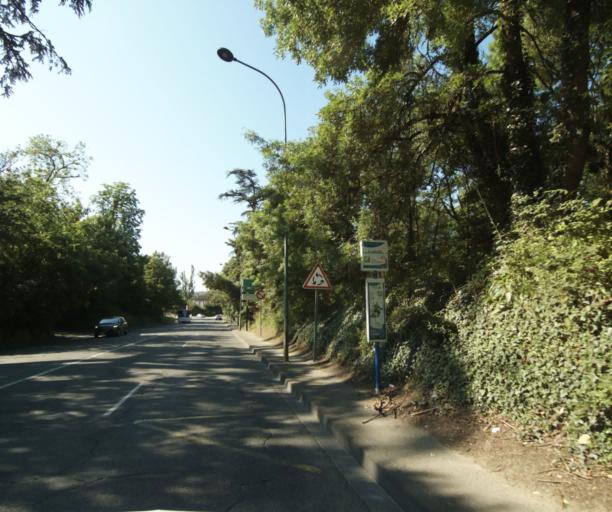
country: FR
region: Midi-Pyrenees
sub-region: Departement du Tarn-et-Garonne
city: Montauban
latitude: 44.0056
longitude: 1.3615
